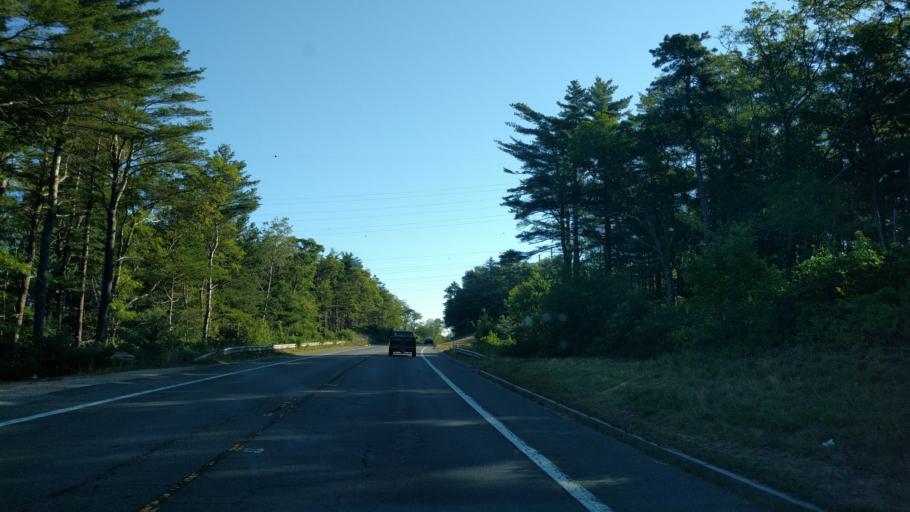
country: US
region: Massachusetts
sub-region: Barnstable County
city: Sagamore
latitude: 41.7651
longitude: -70.5652
